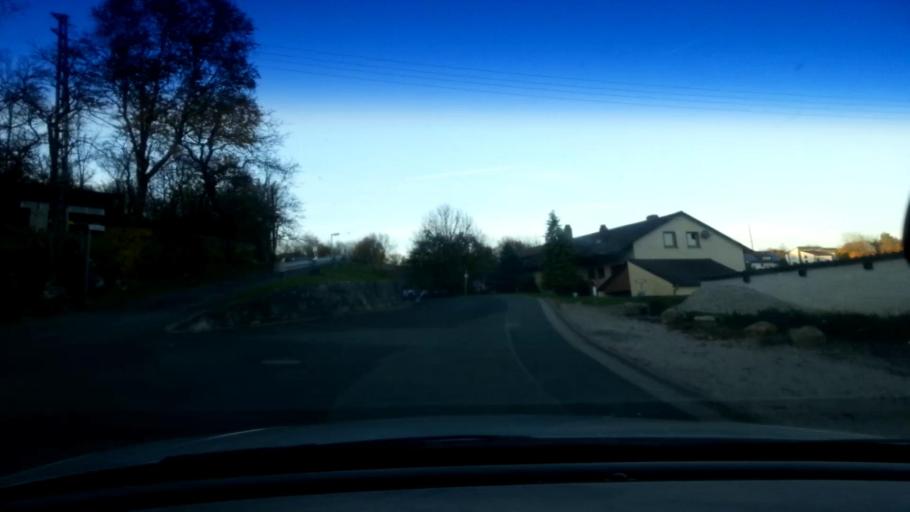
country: DE
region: Bavaria
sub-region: Upper Franconia
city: Heiligenstadt
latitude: 49.8364
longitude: 11.1579
